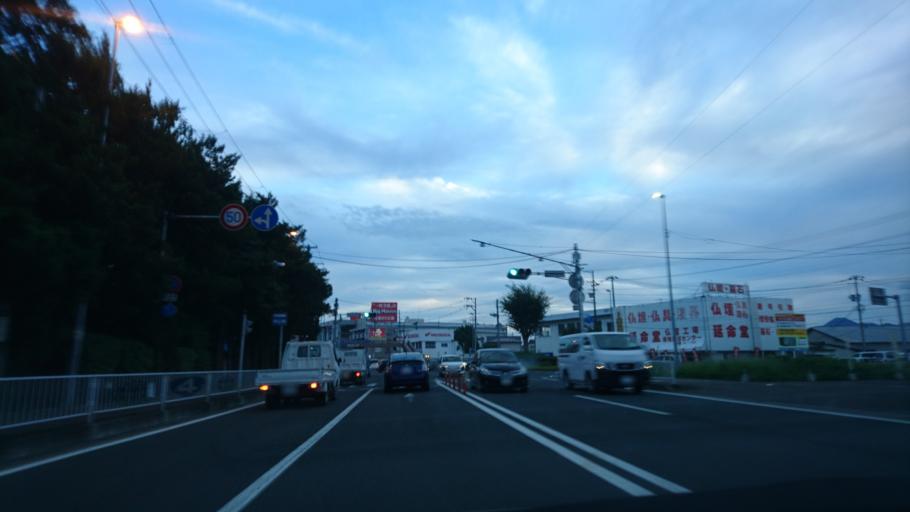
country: JP
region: Iwate
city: Morioka-shi
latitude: 39.6734
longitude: 141.1555
